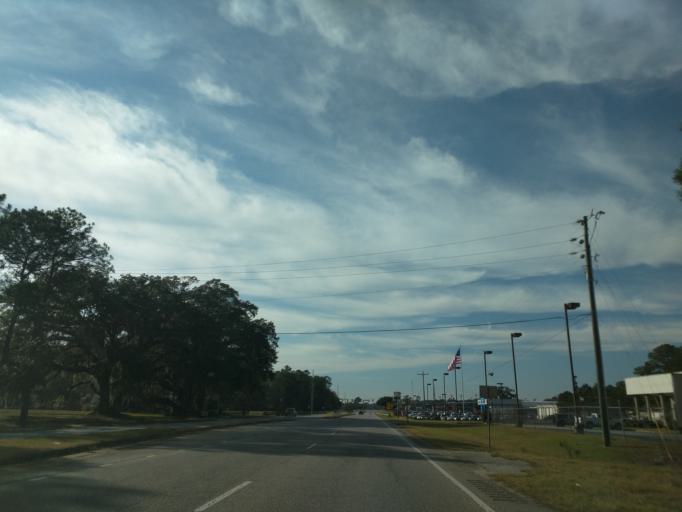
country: US
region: Georgia
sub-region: Decatur County
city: Bainbridge
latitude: 30.9025
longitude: -84.5327
